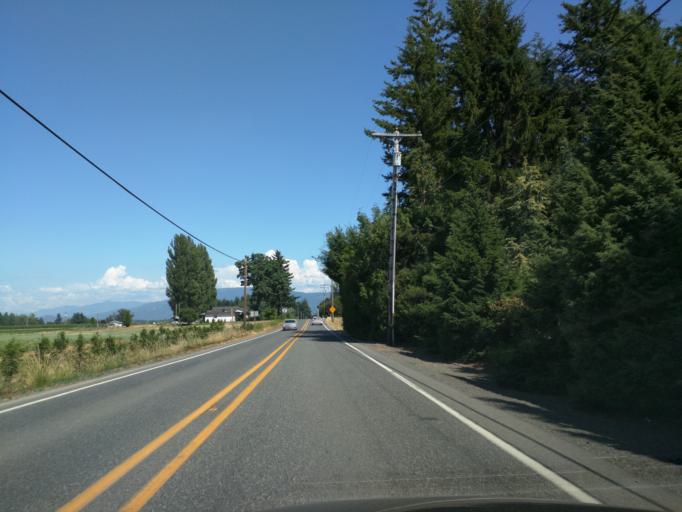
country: US
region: Washington
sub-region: Whatcom County
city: Lynden
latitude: 48.8918
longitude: -122.4322
